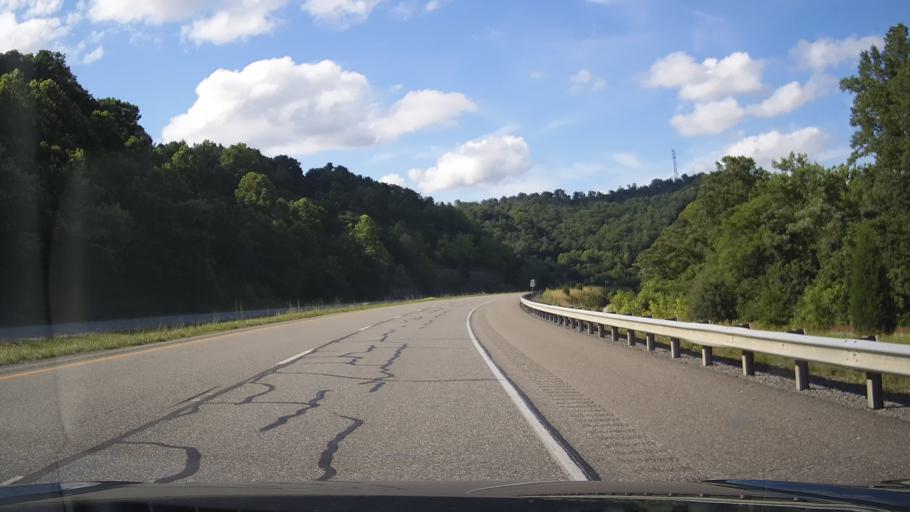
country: US
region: Kentucky
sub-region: Lawrence County
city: Louisa
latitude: 38.1646
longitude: -82.6454
